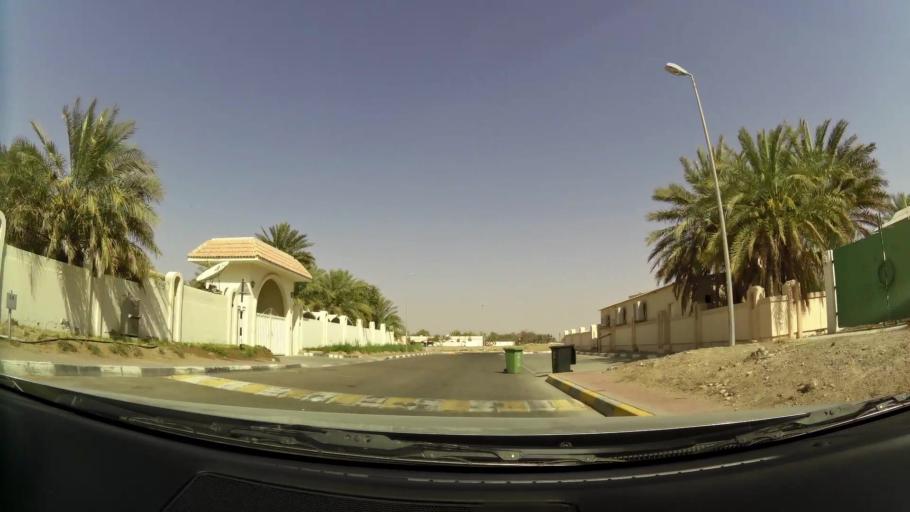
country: OM
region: Al Buraimi
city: Al Buraymi
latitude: 24.3128
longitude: 55.8025
